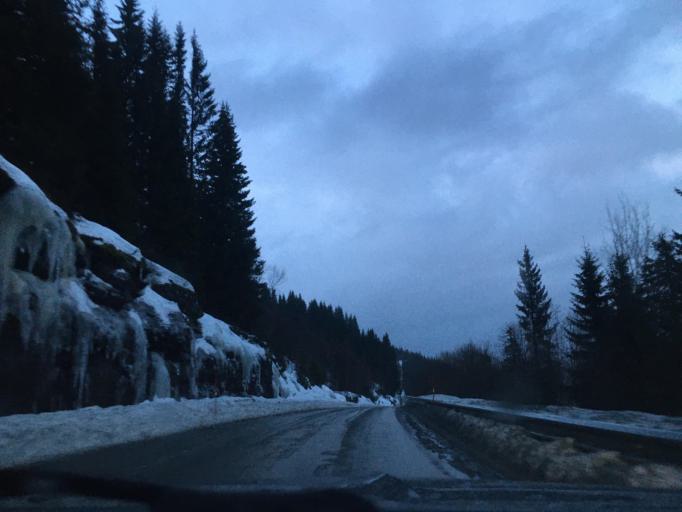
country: NO
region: Nordland
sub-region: Rana
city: Hauknes
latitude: 66.2918
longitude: 13.9144
